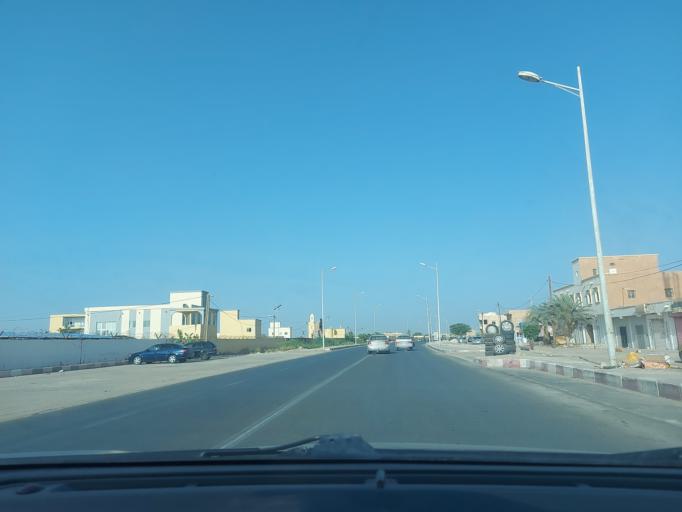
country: MR
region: Nouakchott
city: Nouakchott
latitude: 18.0846
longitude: -15.9931
